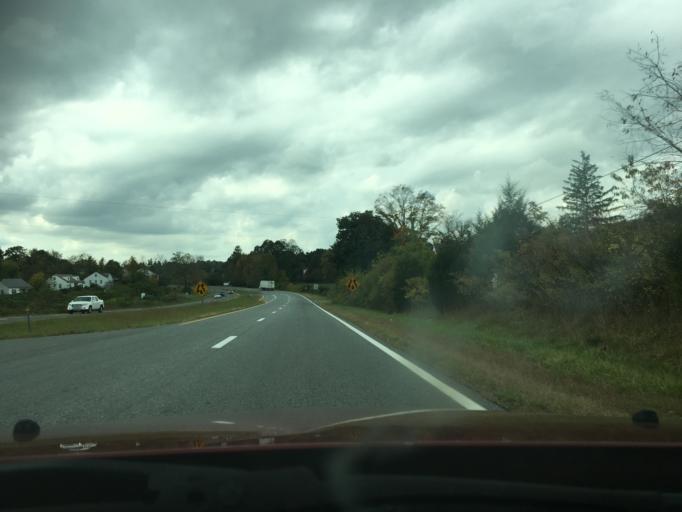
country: US
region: Virginia
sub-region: Pulaski County
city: Fairlawn
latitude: 37.1545
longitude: -80.5736
